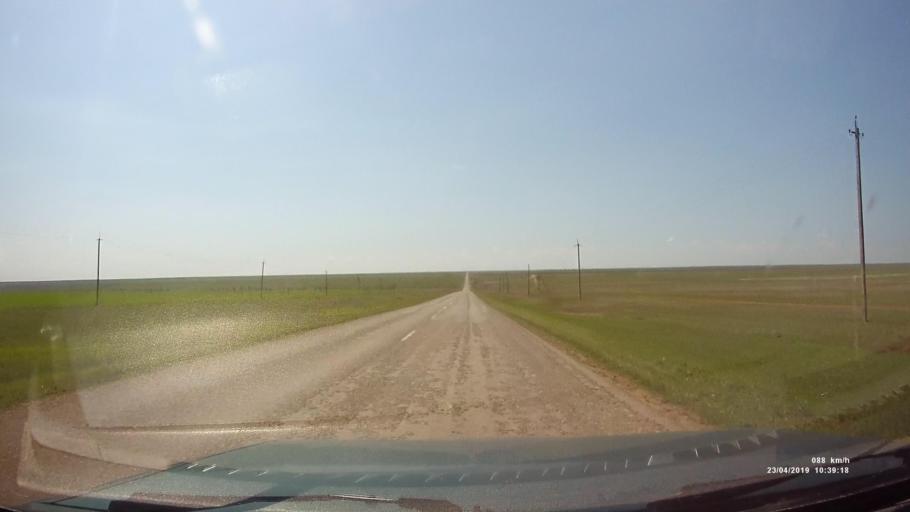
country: RU
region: Kalmykiya
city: Yashalta
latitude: 46.5210
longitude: 42.6387
